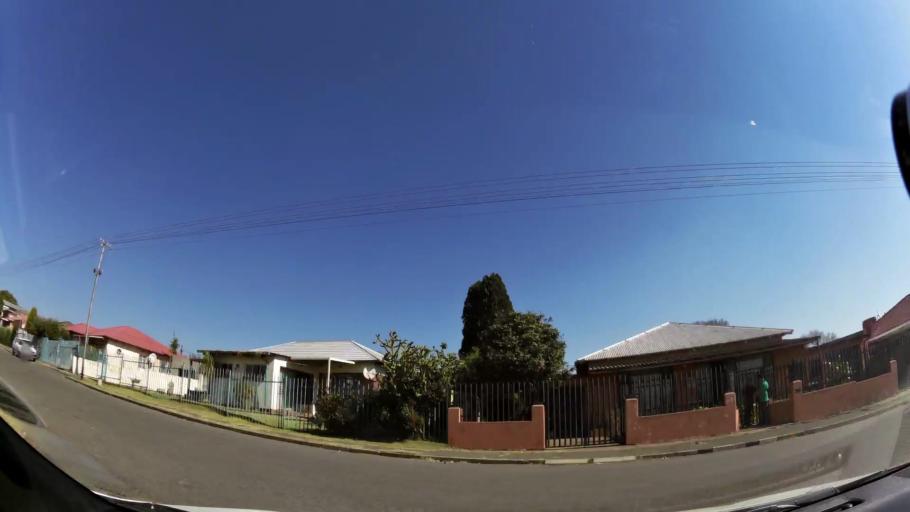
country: ZA
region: Gauteng
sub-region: City of Johannesburg Metropolitan Municipality
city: Johannesburg
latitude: -26.2470
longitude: 28.0893
